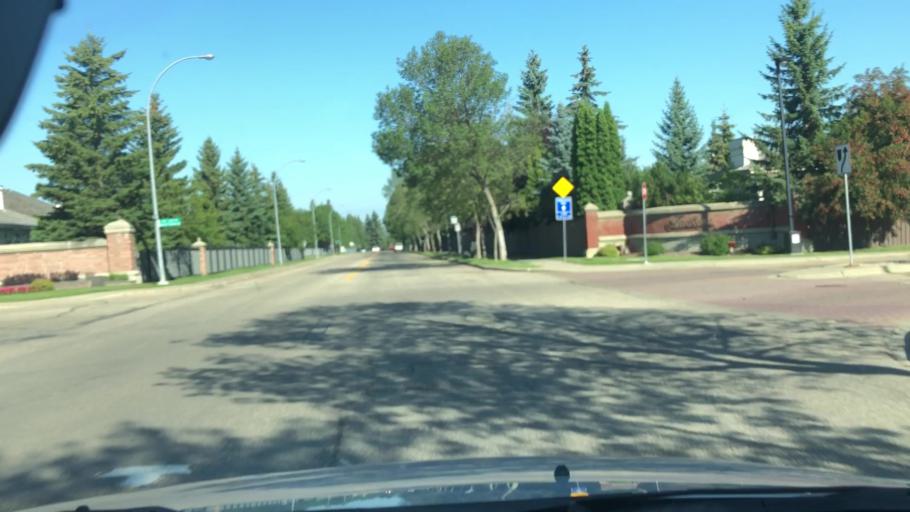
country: CA
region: Alberta
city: Edmonton
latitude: 53.4744
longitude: -113.5984
